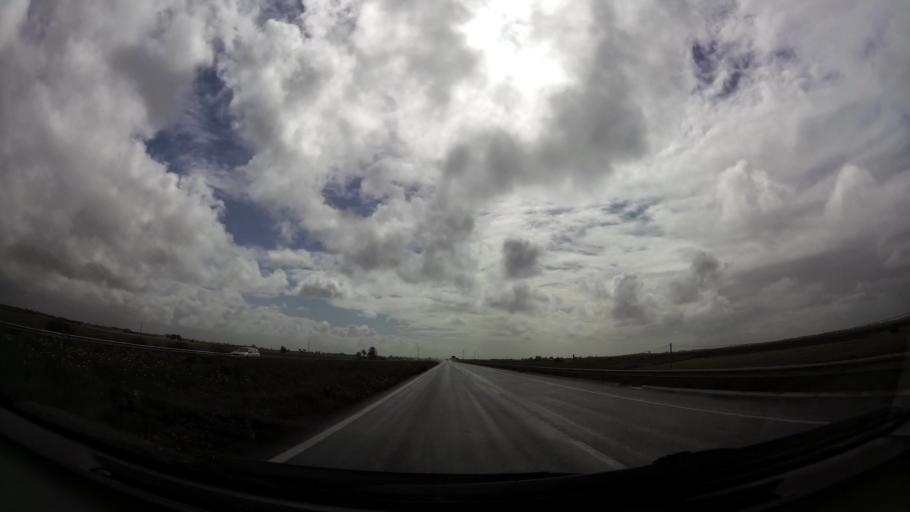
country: MA
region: Grand Casablanca
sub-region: Nouaceur
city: Dar Bouazza
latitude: 33.3626
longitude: -7.9384
